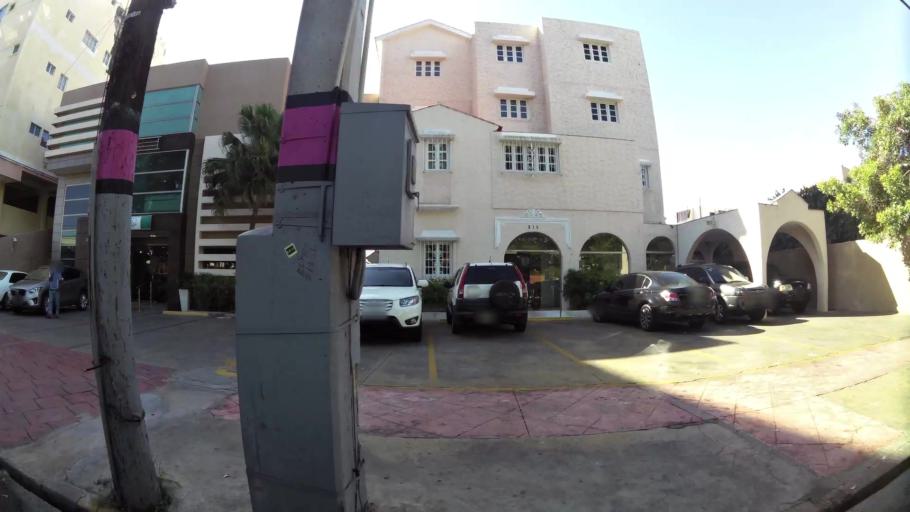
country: DO
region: Nacional
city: Ciudad Nueva
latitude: 18.4699
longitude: -69.9001
